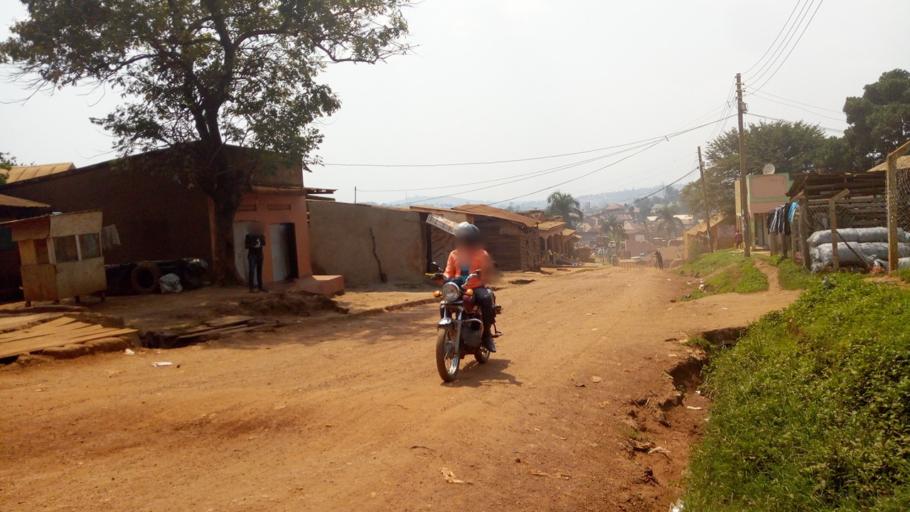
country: UG
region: Central Region
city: Kampala Central Division
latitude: 0.3438
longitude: 32.5551
